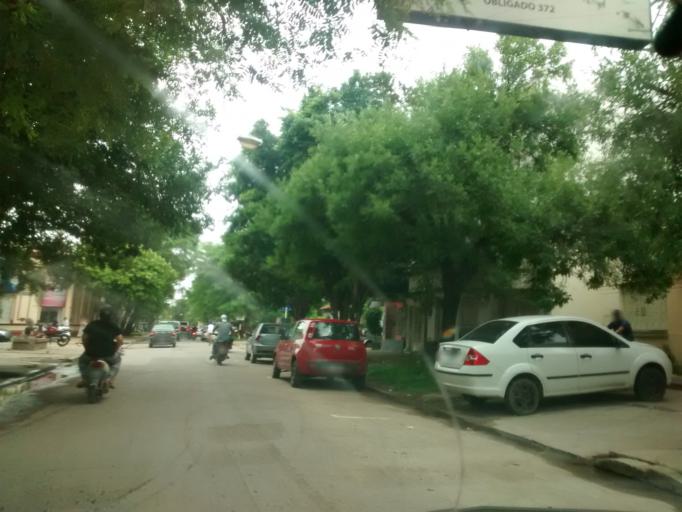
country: AR
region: Chaco
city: Resistencia
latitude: -27.4562
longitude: -58.9860
